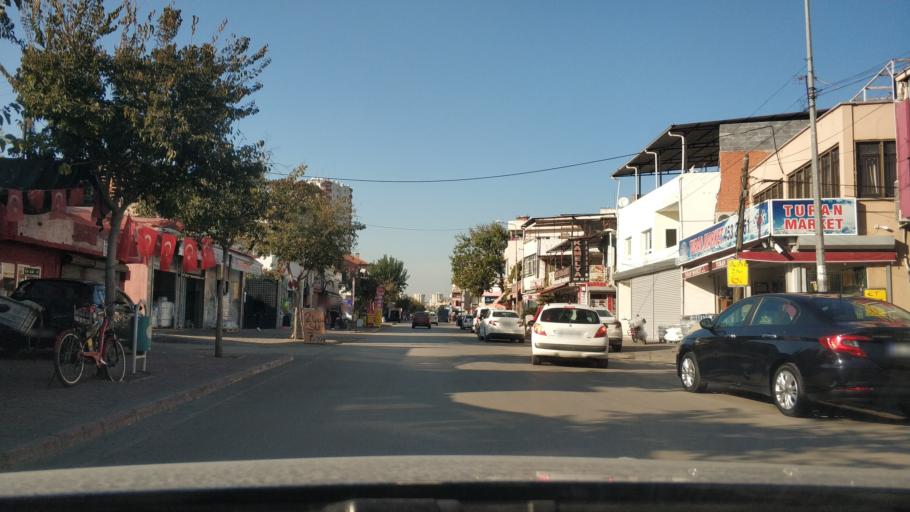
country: TR
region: Adana
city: Seyhan
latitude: 37.0090
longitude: 35.3075
